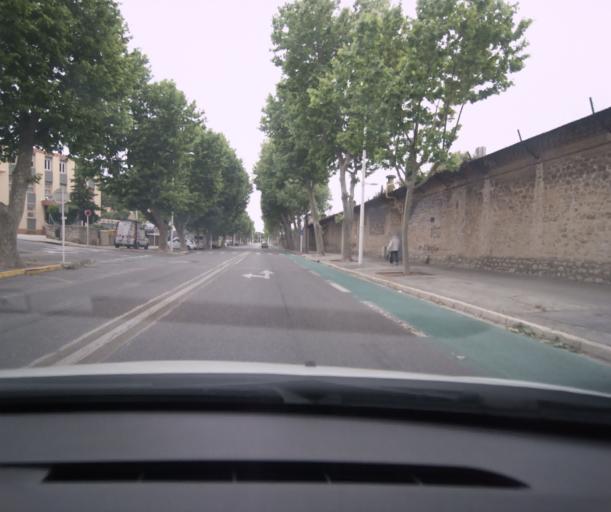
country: FR
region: Provence-Alpes-Cote d'Azur
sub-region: Departement du Var
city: Toulon
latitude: 43.1109
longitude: 5.9324
